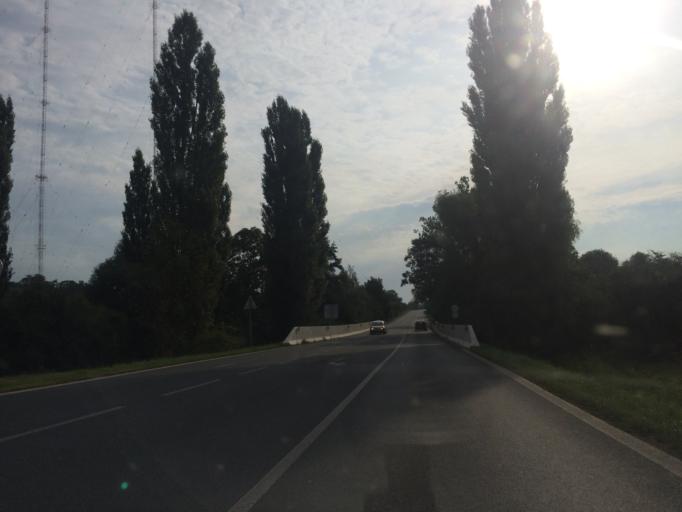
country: CZ
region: Central Bohemia
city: Cesky Brod
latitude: 50.0604
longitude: 14.8796
